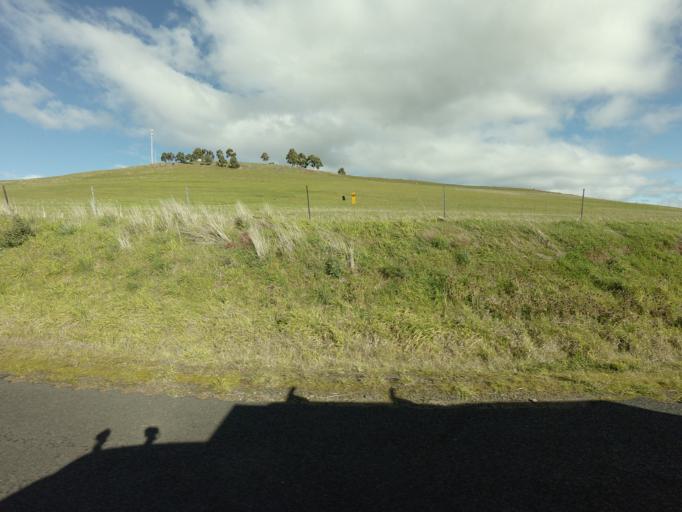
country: AU
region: Tasmania
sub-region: Derwent Valley
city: New Norfolk
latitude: -42.6930
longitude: 146.9446
